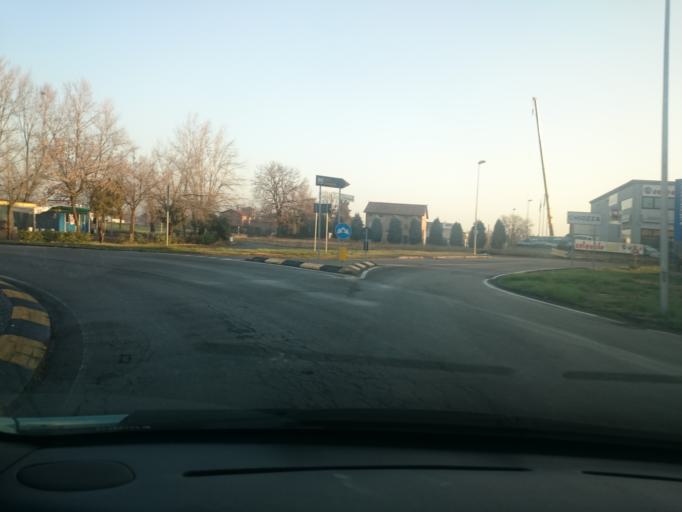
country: IT
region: Emilia-Romagna
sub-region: Provincia di Reggio Emilia
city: Scandiano
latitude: 44.6005
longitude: 10.7042
